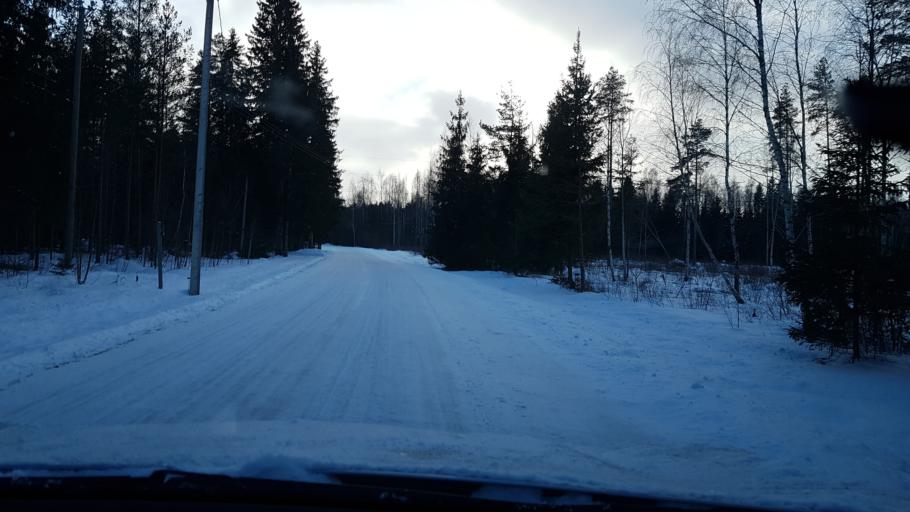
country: EE
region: Harju
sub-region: Nissi vald
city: Turba
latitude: 59.2139
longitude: 24.1412
